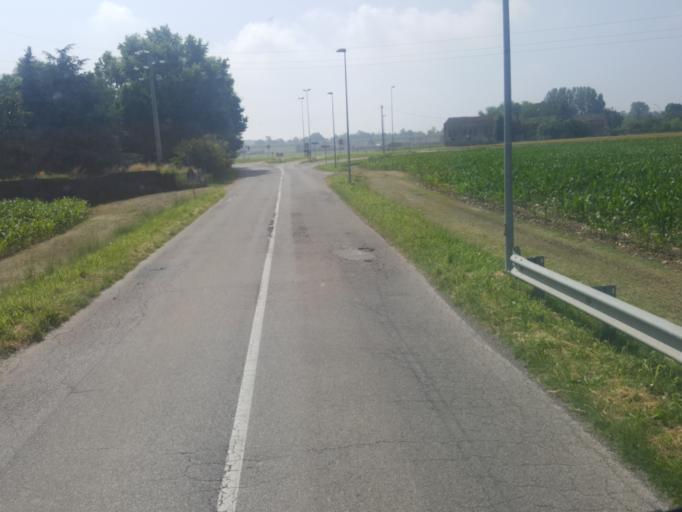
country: IT
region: Veneto
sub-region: Provincia di Rovigo
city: Canaro
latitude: 44.9264
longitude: 11.6877
